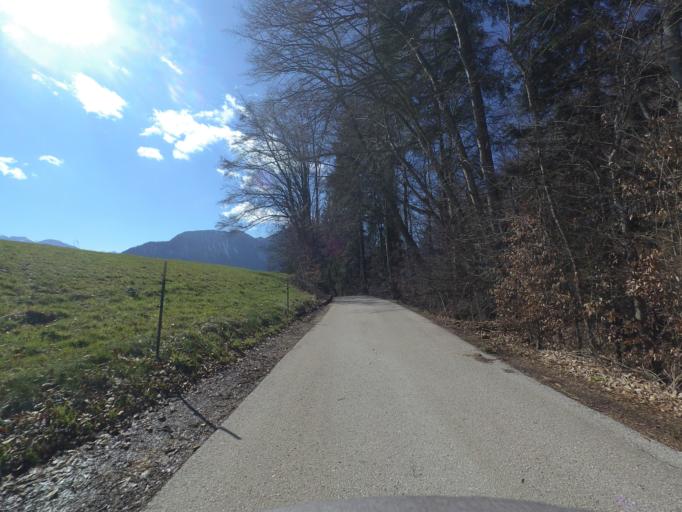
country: DE
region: Bavaria
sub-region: Upper Bavaria
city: Piding
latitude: 47.7868
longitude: 12.9192
